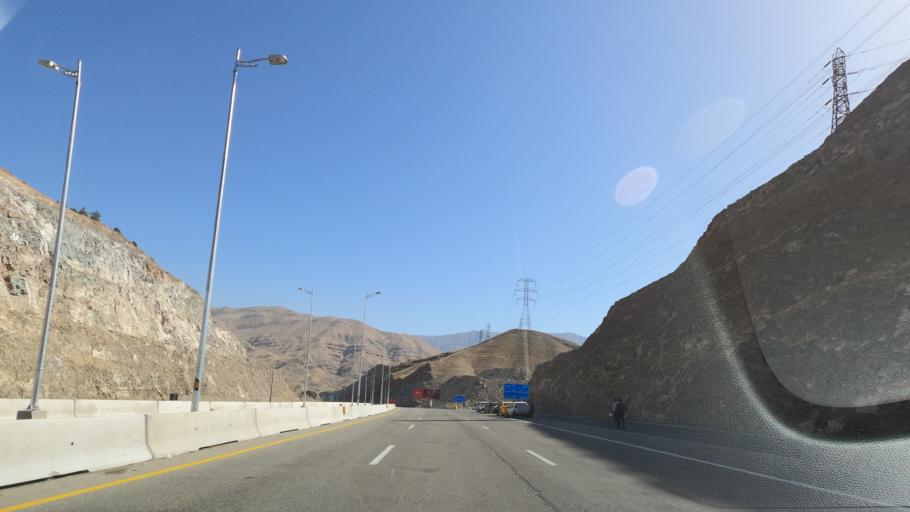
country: IR
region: Alborz
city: Karaj
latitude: 35.8138
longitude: 51.0371
